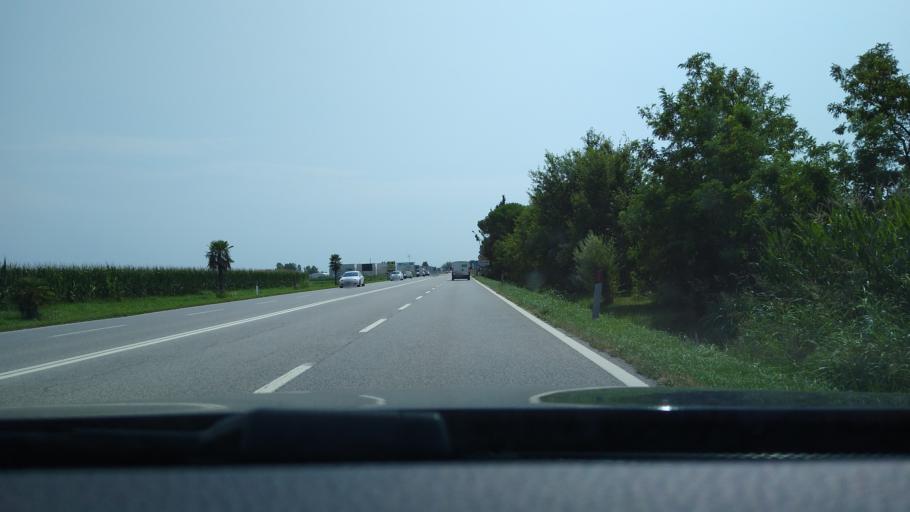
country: IT
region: Friuli Venezia Giulia
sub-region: Provincia di Udine
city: Pertegada
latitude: 45.7355
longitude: 13.0416
